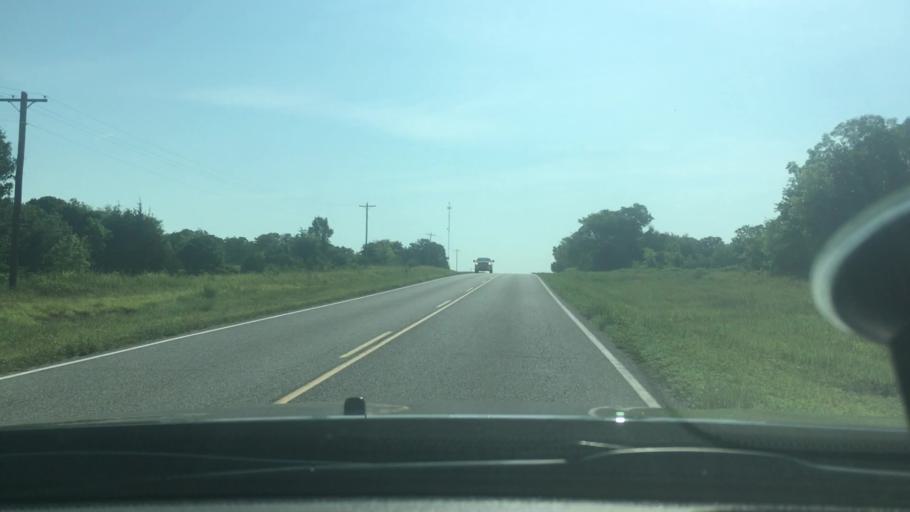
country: US
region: Oklahoma
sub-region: Garvin County
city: Pauls Valley
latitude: 34.6517
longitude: -97.2705
